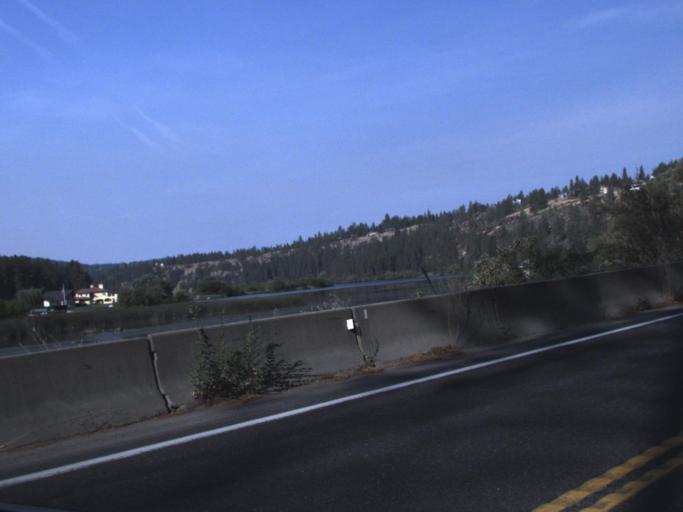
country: US
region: Washington
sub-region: Spokane County
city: Fairwood
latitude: 47.8007
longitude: -117.5430
